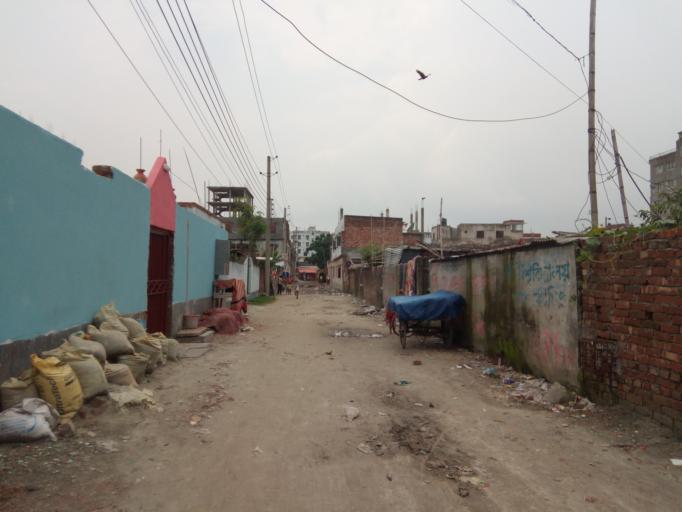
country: BD
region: Dhaka
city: Azimpur
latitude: 23.7572
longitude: 90.3510
